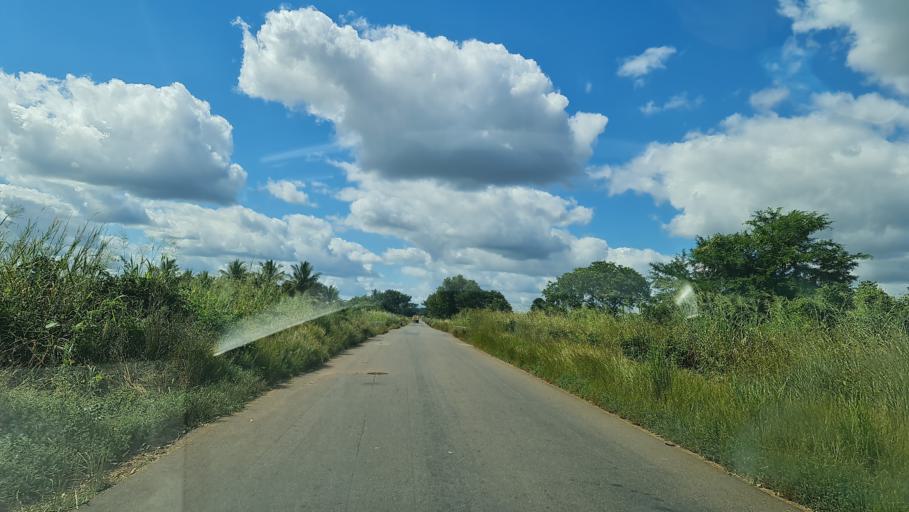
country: MZ
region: Zambezia
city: Quelimane
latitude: -17.5160
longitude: 36.2204
